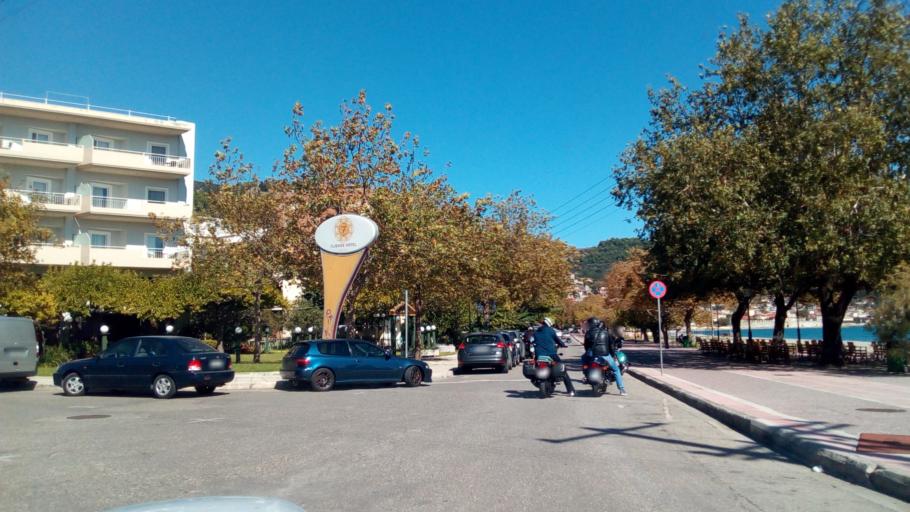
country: GR
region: West Greece
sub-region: Nomos Aitolias kai Akarnanias
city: Nafpaktos
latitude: 38.3878
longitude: 21.8214
